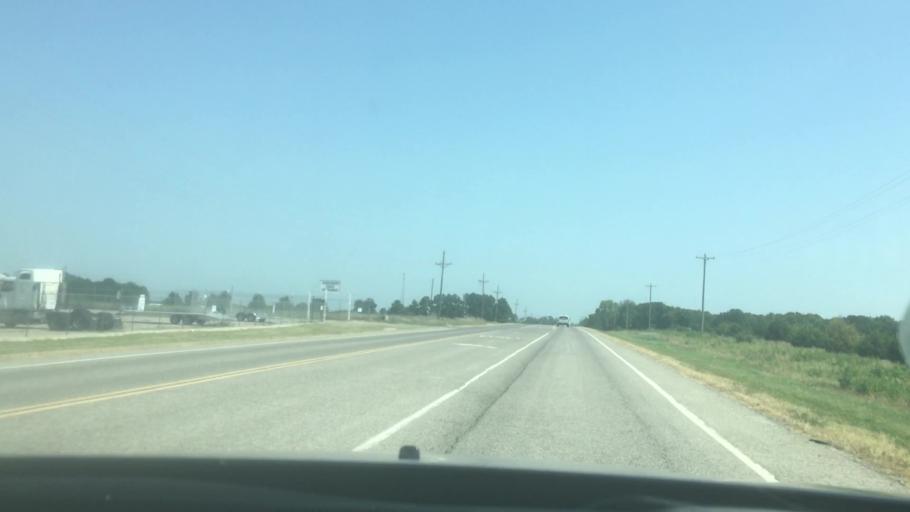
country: US
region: Oklahoma
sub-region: Bryan County
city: Durant
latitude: 34.2326
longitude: -96.4248
